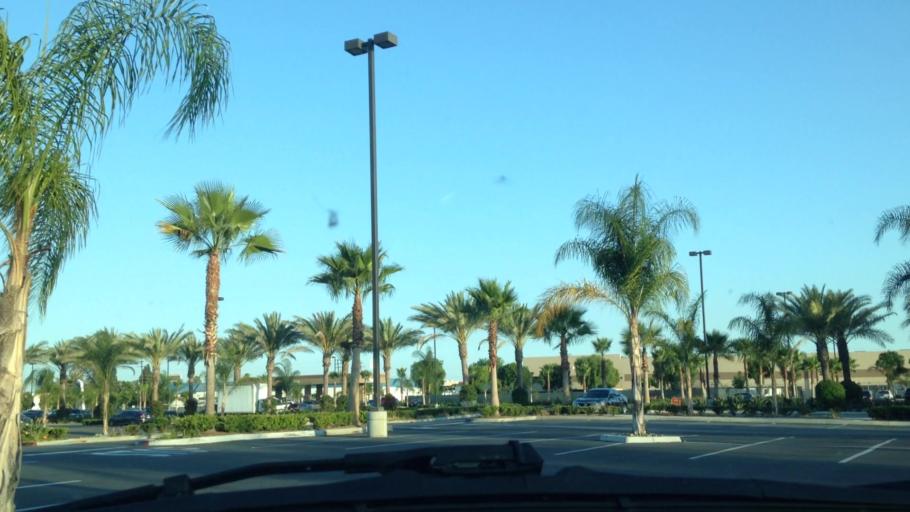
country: US
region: California
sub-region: Orange County
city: Placentia
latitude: 33.8665
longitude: -117.8852
